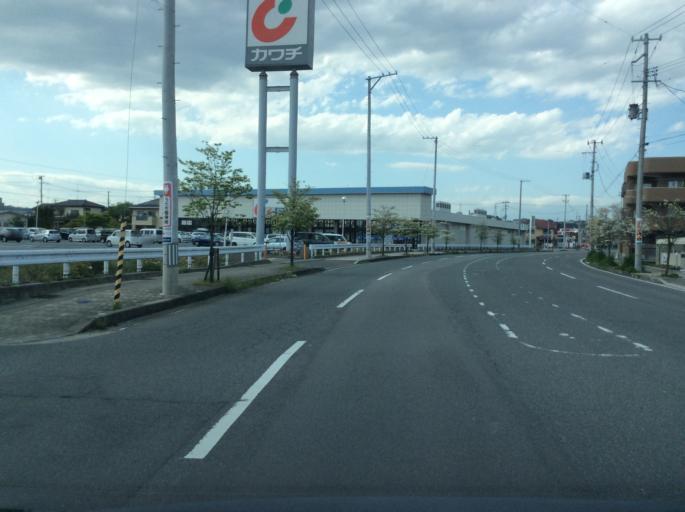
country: JP
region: Fukushima
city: Iwaki
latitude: 36.9509
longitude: 140.8602
